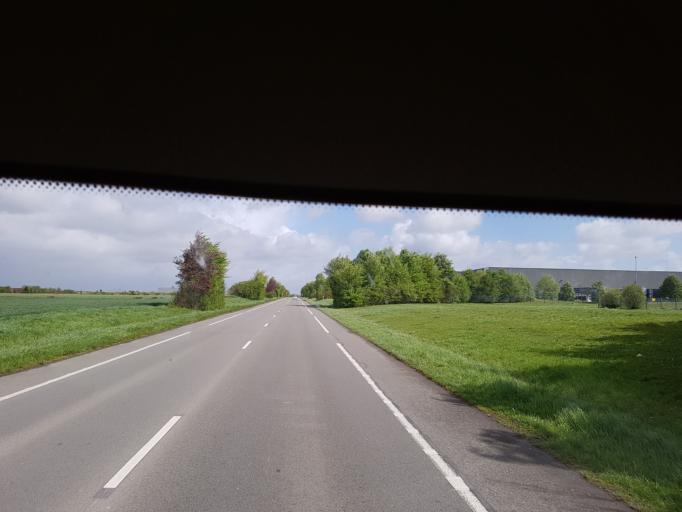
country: FR
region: Nord-Pas-de-Calais
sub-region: Departement du Nord
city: Raillencourt-Sainte-Olle
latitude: 50.1911
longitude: 3.1904
